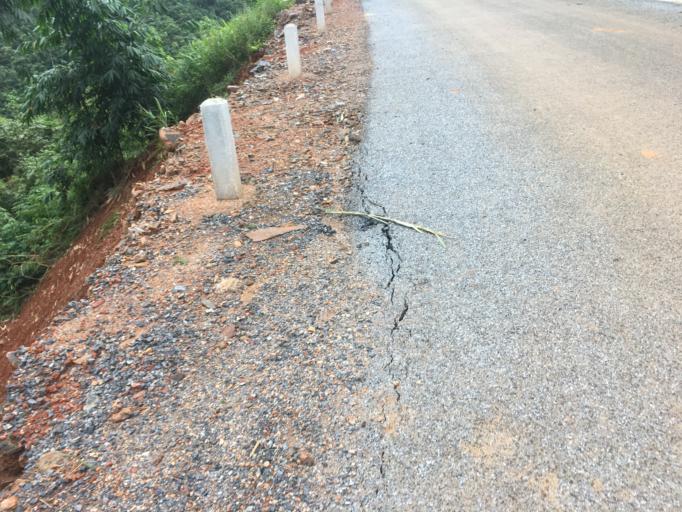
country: VN
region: Ha Giang
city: Thi Tran Tam Son
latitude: 22.9548
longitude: 105.0378
